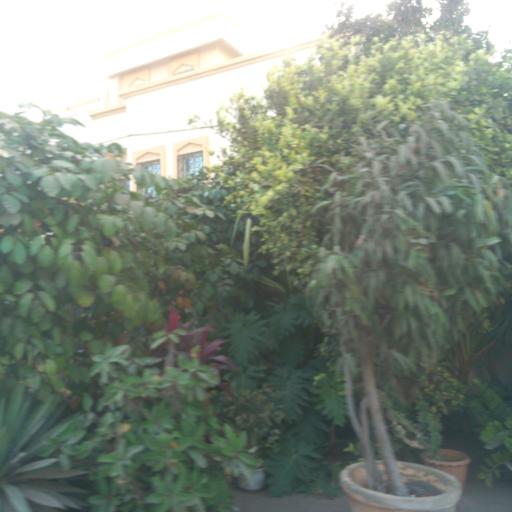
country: SN
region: Dakar
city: Grand Dakar
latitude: 14.7171
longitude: -17.4663
